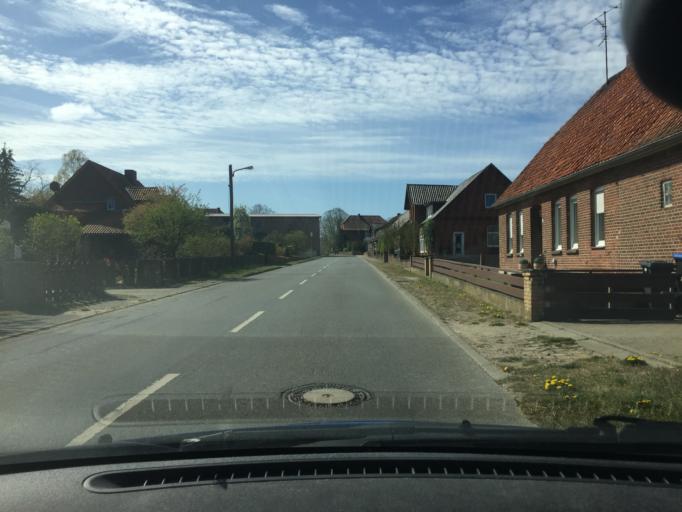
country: DE
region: Lower Saxony
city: Ratzlingen
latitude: 52.9593
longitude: 10.6684
